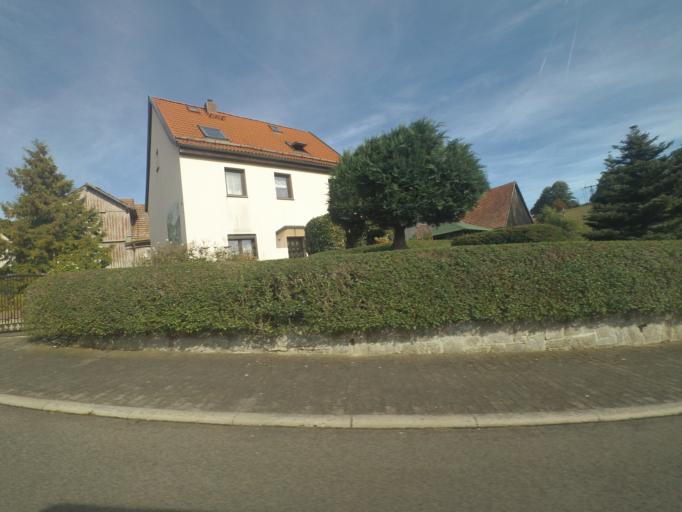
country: DE
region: Thuringia
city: Oberkatz
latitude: 50.5798
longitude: 10.2616
